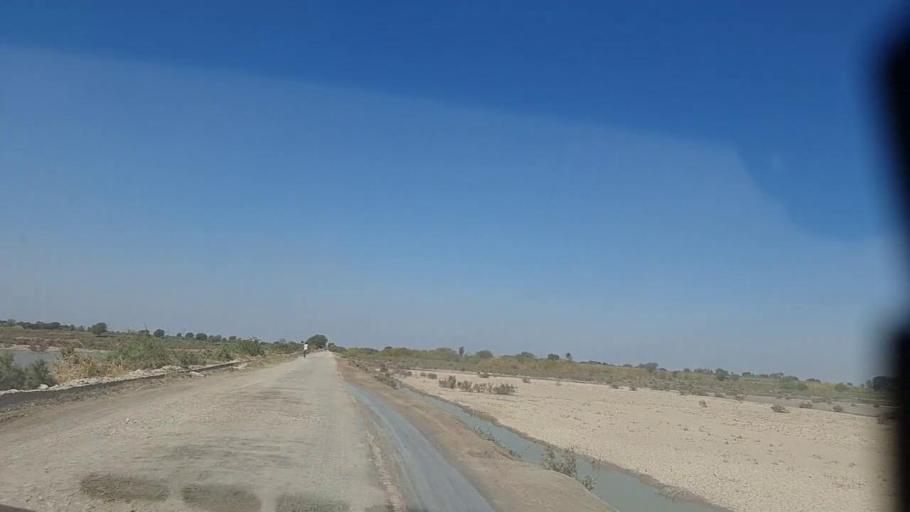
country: PK
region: Sindh
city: Digri
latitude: 25.1696
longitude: 69.0639
